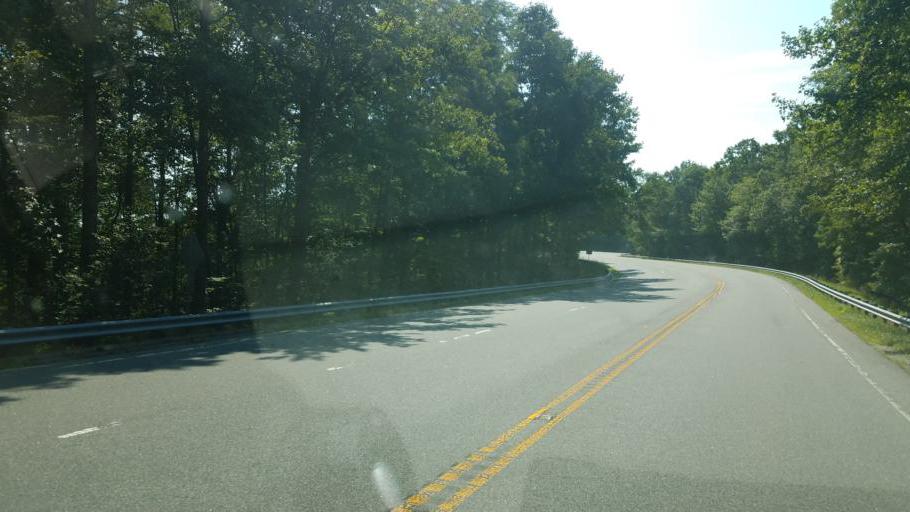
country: US
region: North Carolina
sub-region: Avery County
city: Newland
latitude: 35.9364
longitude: -81.8359
